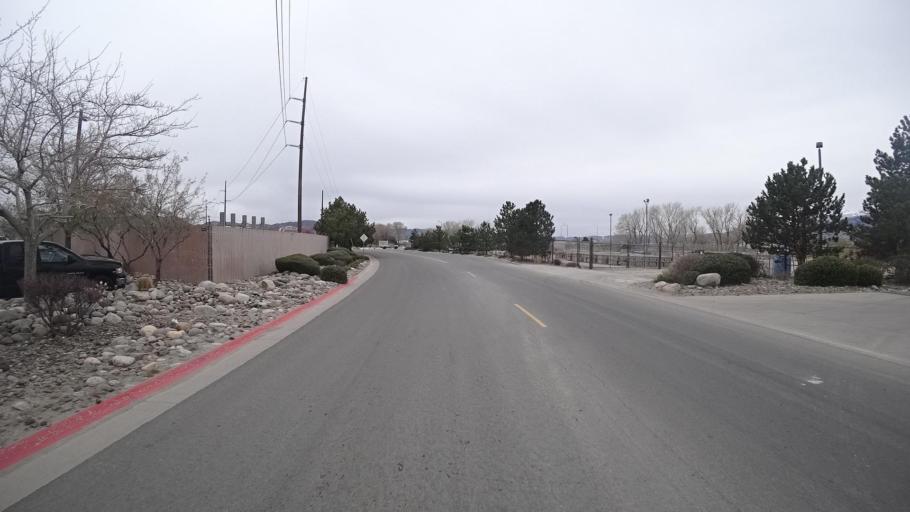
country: US
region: Nevada
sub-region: Washoe County
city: Sparks
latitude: 39.5237
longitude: -119.7712
